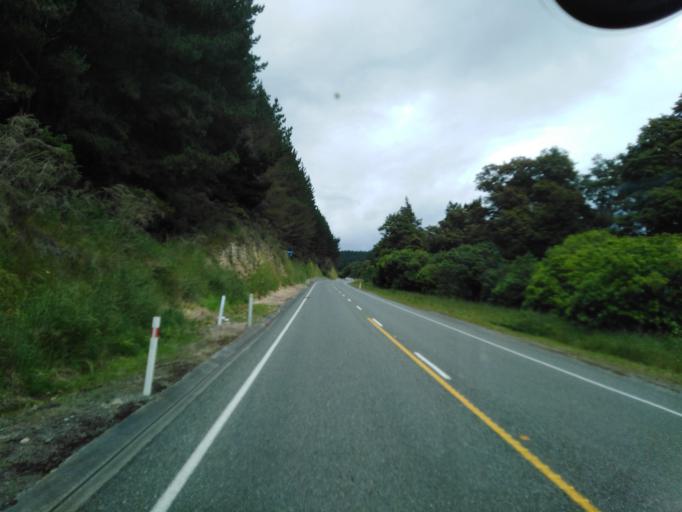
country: NZ
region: Tasman
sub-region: Tasman District
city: Wakefield
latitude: -41.4741
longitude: 172.9367
